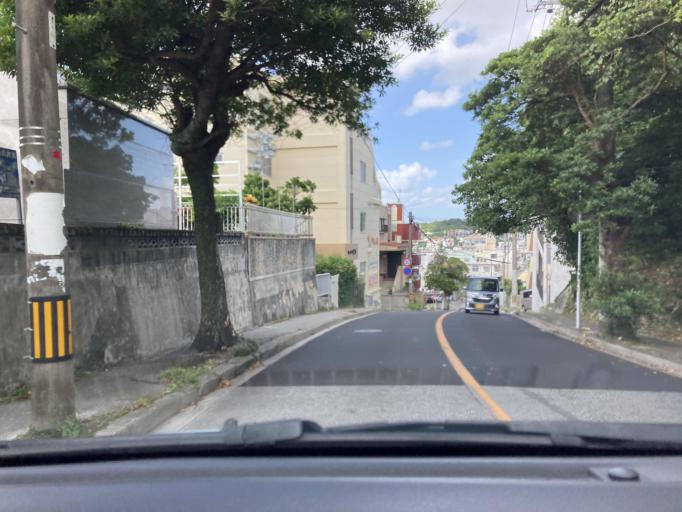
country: JP
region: Okinawa
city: Naha-shi
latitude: 26.2086
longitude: 127.7114
